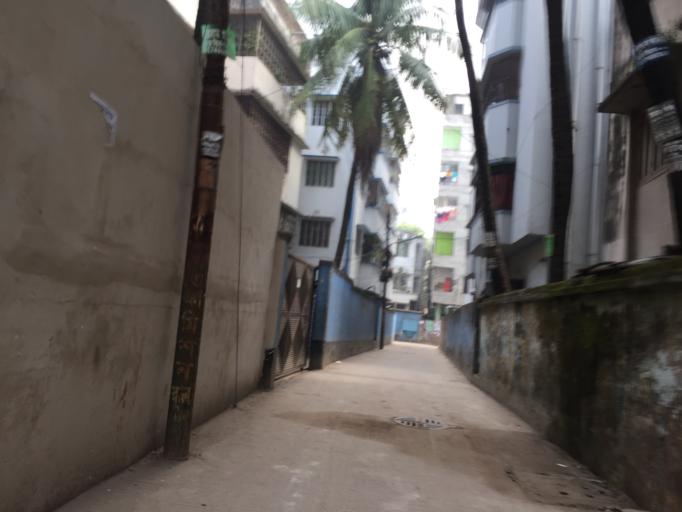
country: BD
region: Dhaka
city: Azimpur
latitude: 23.7857
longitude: 90.3611
